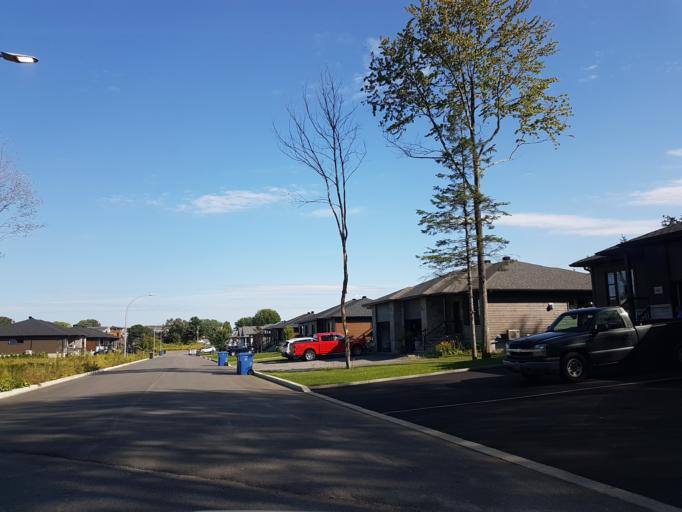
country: CA
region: Quebec
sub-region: Mauricie
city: Nicolet
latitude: 46.2905
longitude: -72.6435
